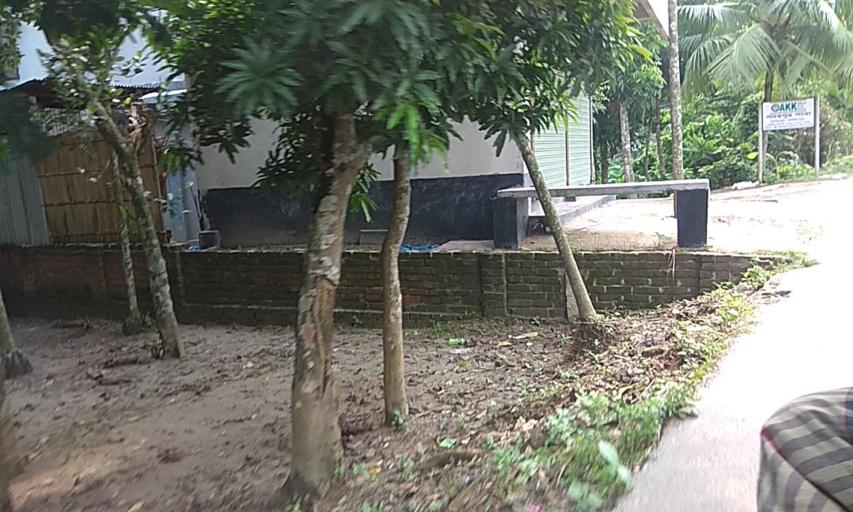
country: BD
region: Dhaka
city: Dohar
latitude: 23.4746
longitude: 90.0331
